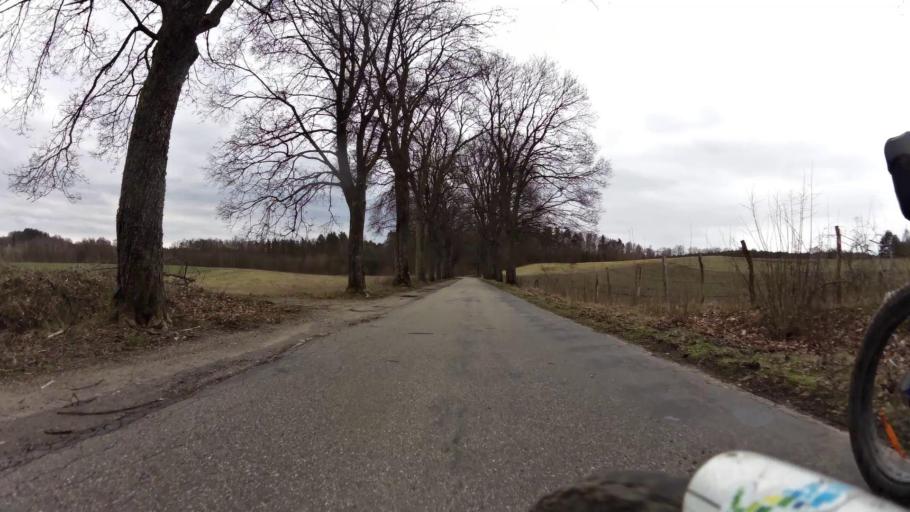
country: PL
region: Pomeranian Voivodeship
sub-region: Powiat bytowski
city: Trzebielino
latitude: 54.1001
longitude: 17.1319
